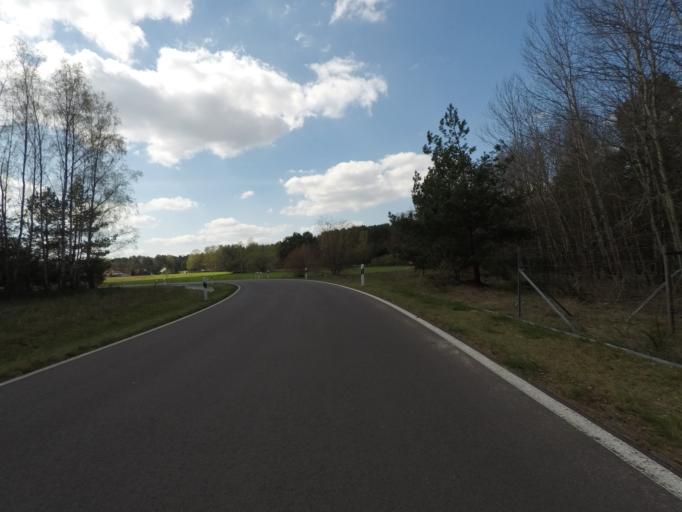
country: DE
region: Brandenburg
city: Melchow
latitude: 52.8354
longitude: 13.7011
